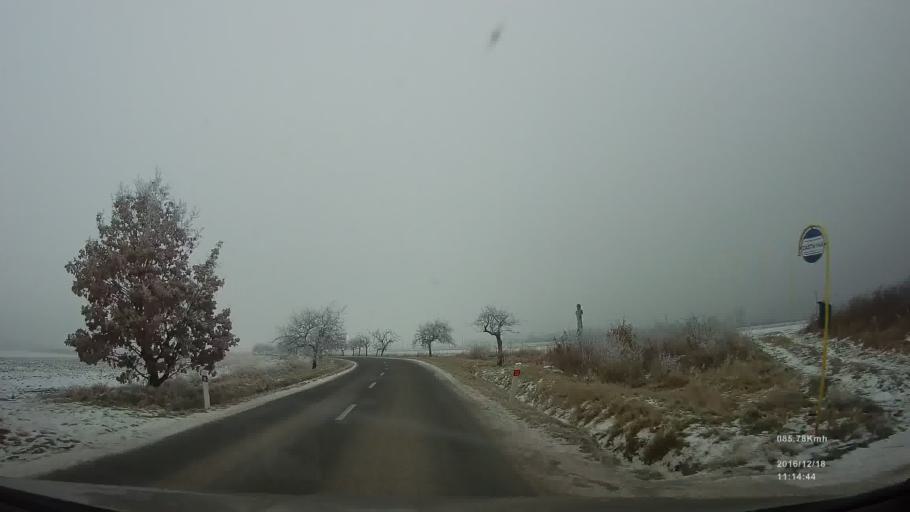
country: SK
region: Presovsky
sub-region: Okres Presov
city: Presov
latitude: 48.8965
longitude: 21.3202
